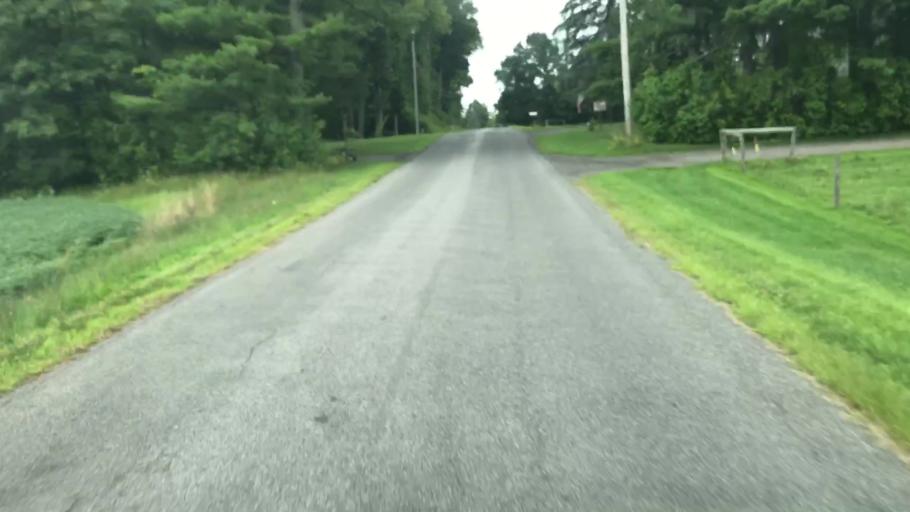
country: US
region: New York
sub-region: Cayuga County
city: Melrose Park
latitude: 42.9588
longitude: -76.5068
